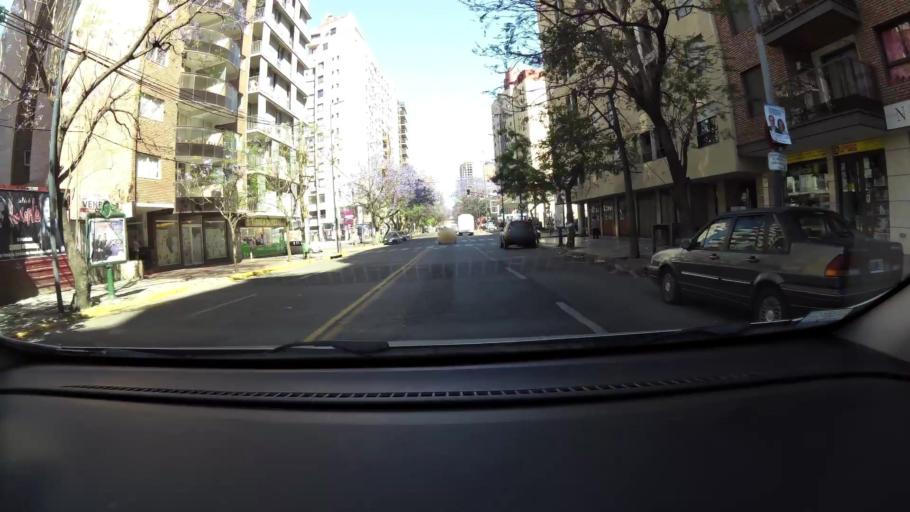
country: AR
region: Cordoba
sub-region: Departamento de Capital
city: Cordoba
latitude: -31.4262
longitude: -64.1926
